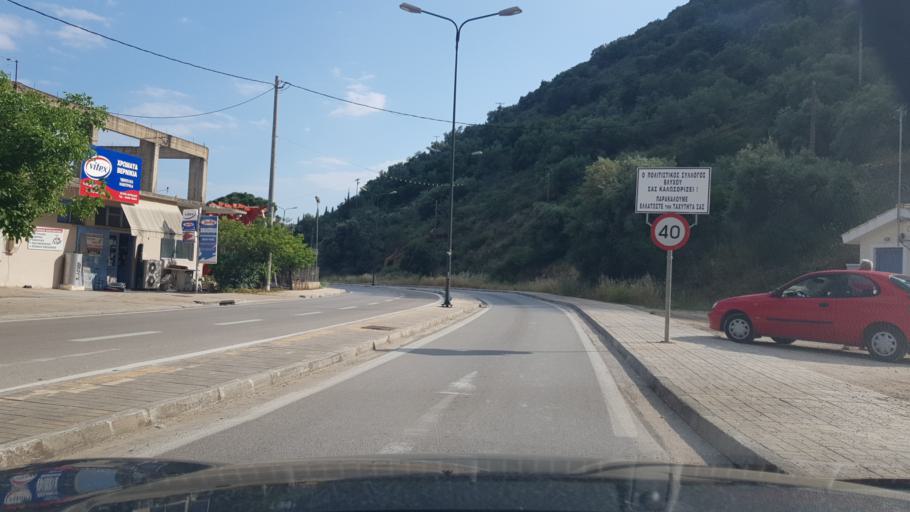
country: GR
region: Ionian Islands
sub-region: Lefkada
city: Nidri
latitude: 38.6913
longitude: 20.6985
